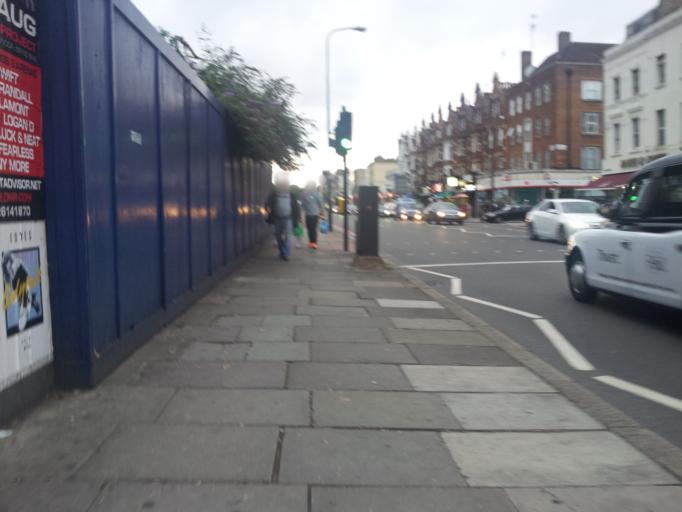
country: GB
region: England
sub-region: Greater London
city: Bayswater
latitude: 51.5206
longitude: -0.1711
